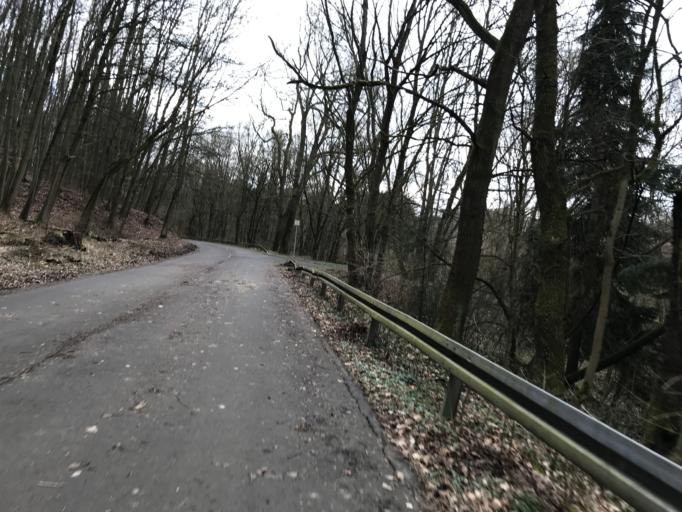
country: DE
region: Hesse
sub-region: Regierungsbezirk Giessen
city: Lich
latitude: 50.5403
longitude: 8.8011
